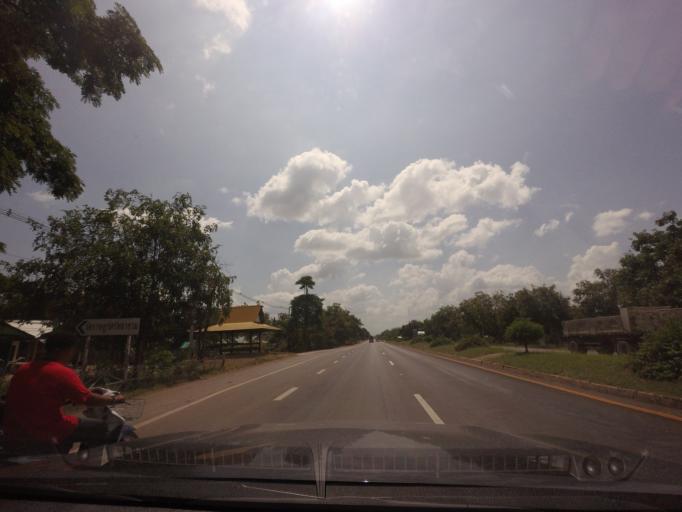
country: TH
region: Phetchabun
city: Nong Phai
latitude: 16.1418
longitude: 101.0537
